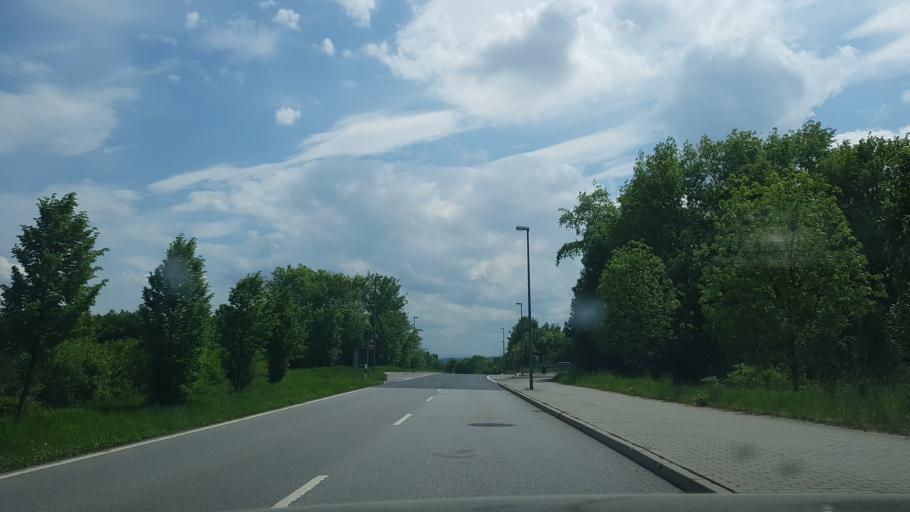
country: DE
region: Saxony
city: Freital
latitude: 51.0324
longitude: 13.6363
